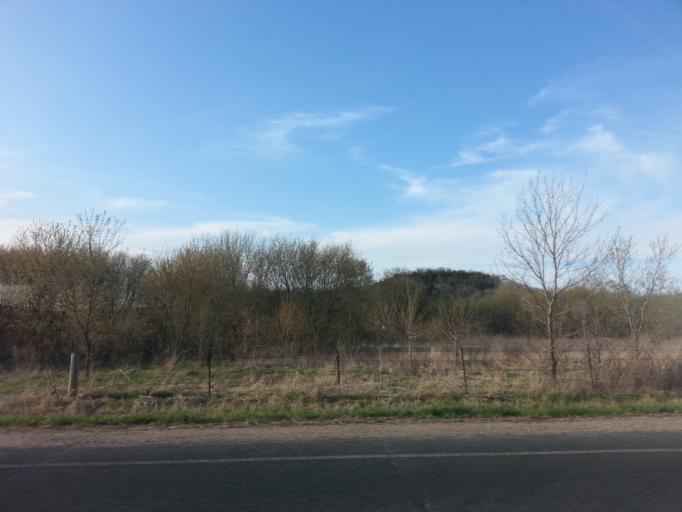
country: US
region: Wisconsin
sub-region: Pierce County
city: River Falls
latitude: 44.8626
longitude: -92.6510
